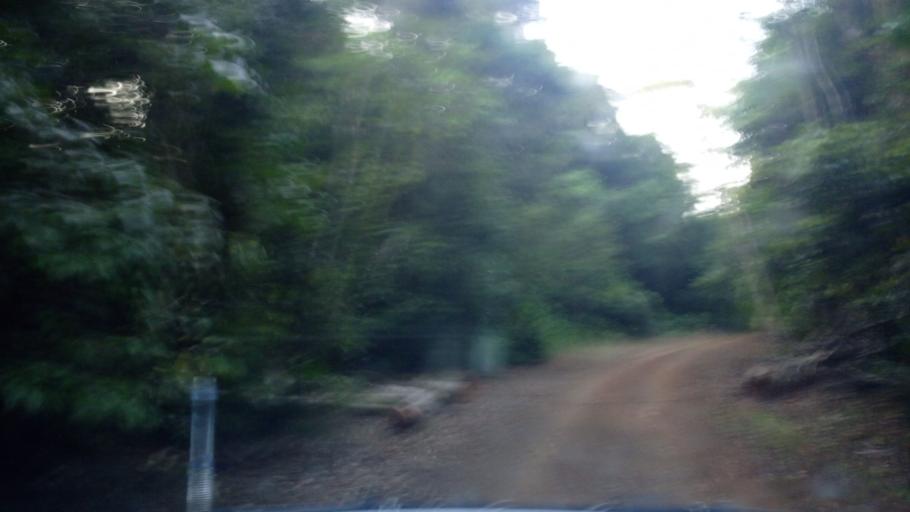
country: AU
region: Queensland
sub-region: Tablelands
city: Atherton
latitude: -17.3710
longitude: 145.7541
